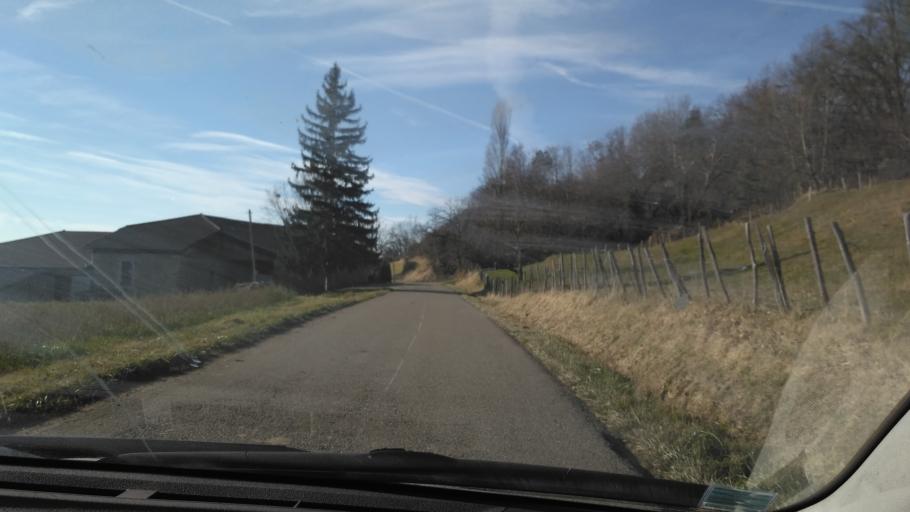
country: FR
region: Rhone-Alpes
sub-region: Departement de l'Isere
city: Saint-Antoine-l'Abbaye
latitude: 45.1619
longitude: 5.1940
